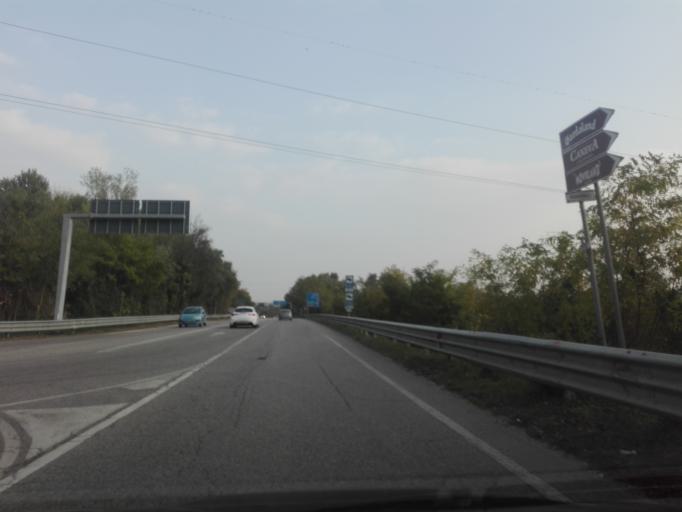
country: IT
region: Veneto
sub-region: Provincia di Verona
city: Cola
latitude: 45.4908
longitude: 10.7657
